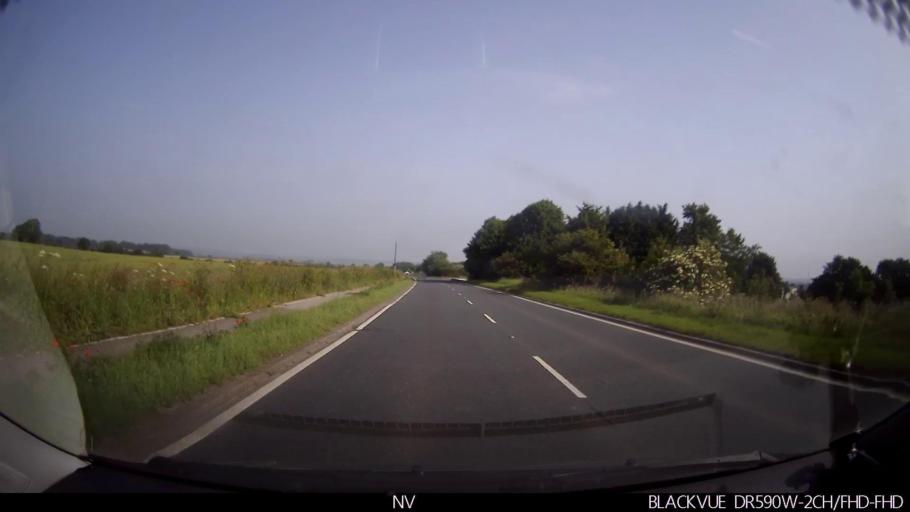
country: GB
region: England
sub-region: North Yorkshire
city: East Ayton
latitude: 54.2106
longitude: -0.4362
